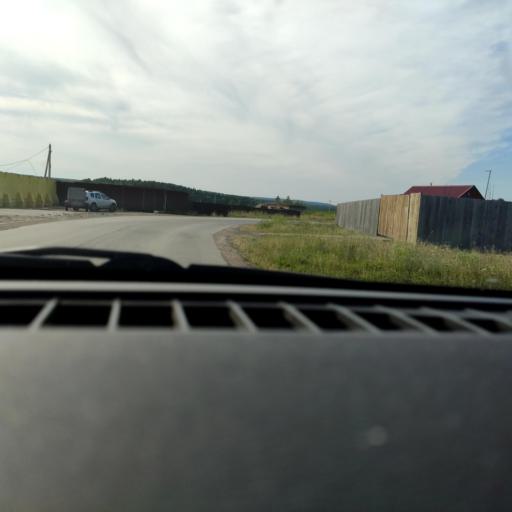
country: RU
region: Perm
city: Polazna
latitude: 58.3524
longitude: 56.2439
